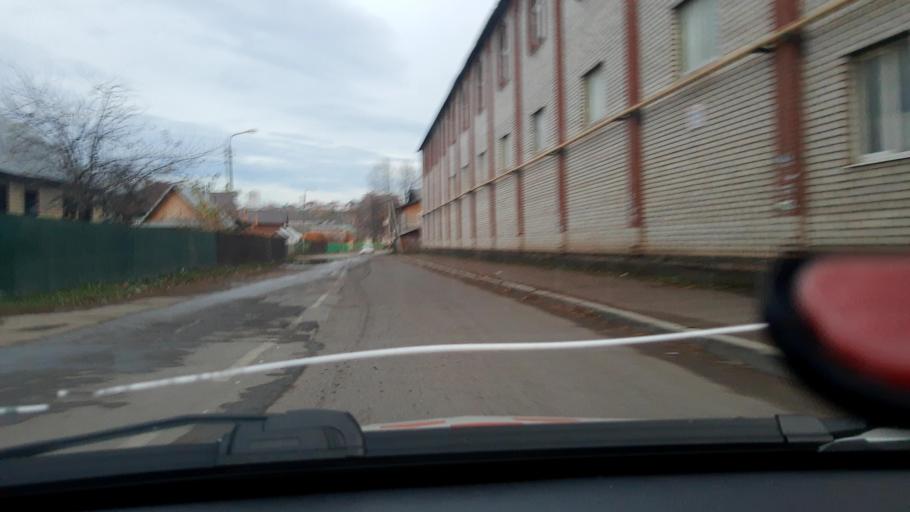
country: RU
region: Bashkortostan
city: Ufa
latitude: 54.7293
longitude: 55.8975
